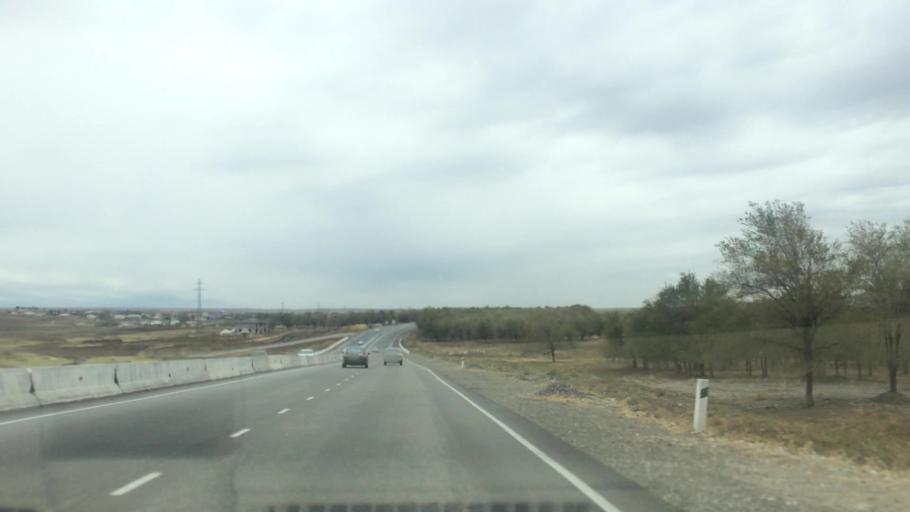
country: UZ
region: Samarqand
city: Bulung'ur
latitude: 39.9224
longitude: 67.5168
